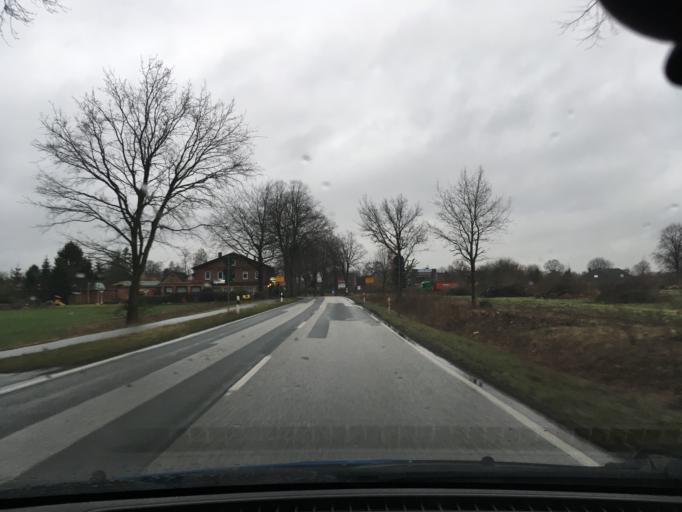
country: DE
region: Schleswig-Holstein
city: Wiershop
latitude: 53.4049
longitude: 10.4479
